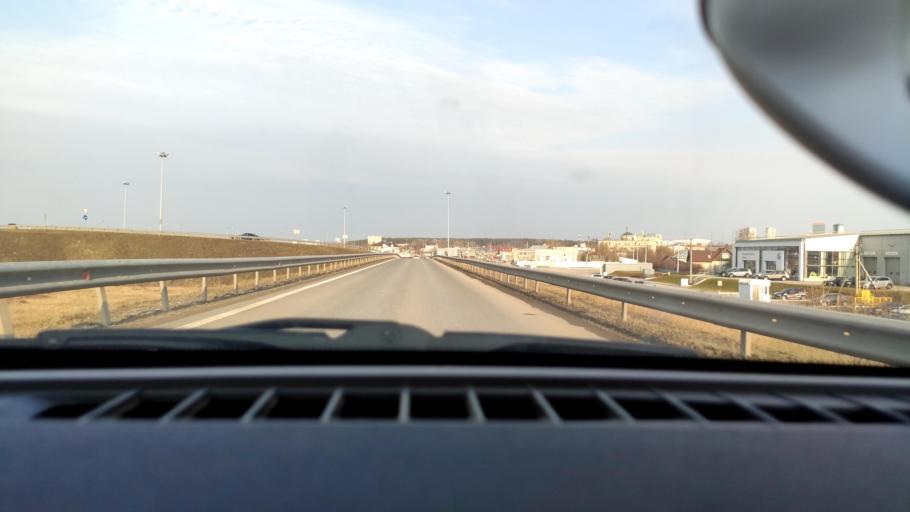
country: RU
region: Perm
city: Kondratovo
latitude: 57.9528
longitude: 56.1233
